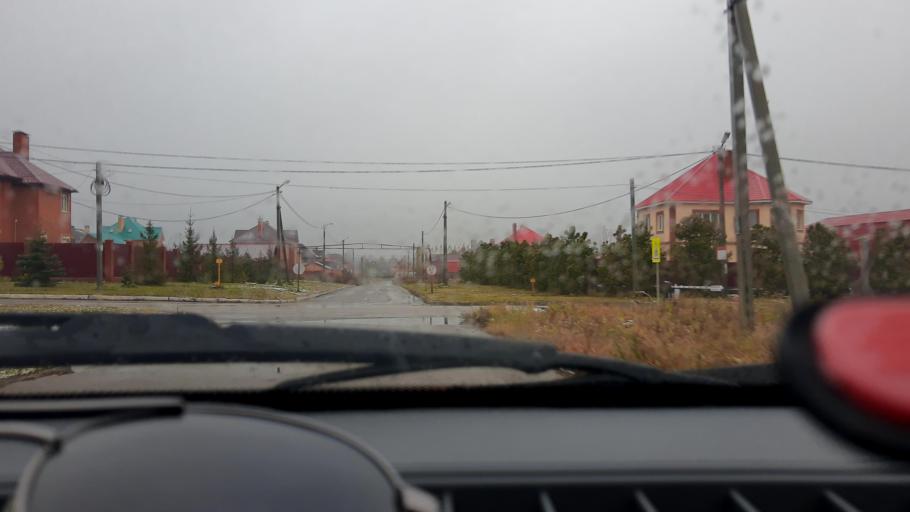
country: RU
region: Bashkortostan
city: Kabakovo
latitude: 54.6221
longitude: 56.1297
